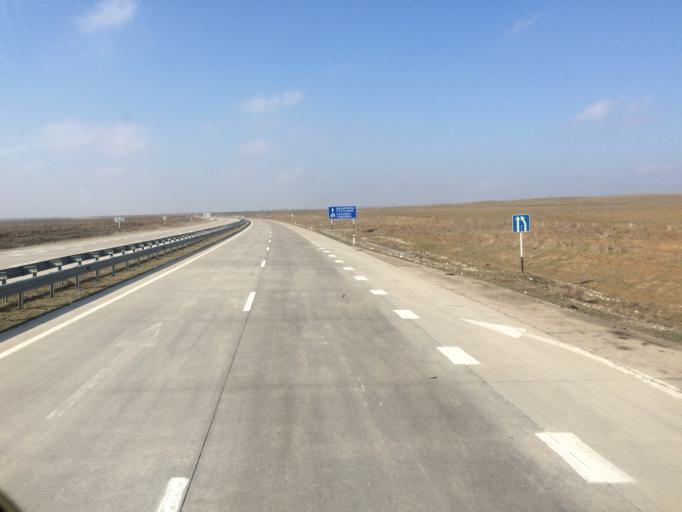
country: KZ
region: Ongtustik Qazaqstan
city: Shymkent
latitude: 42.4886
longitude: 69.5178
